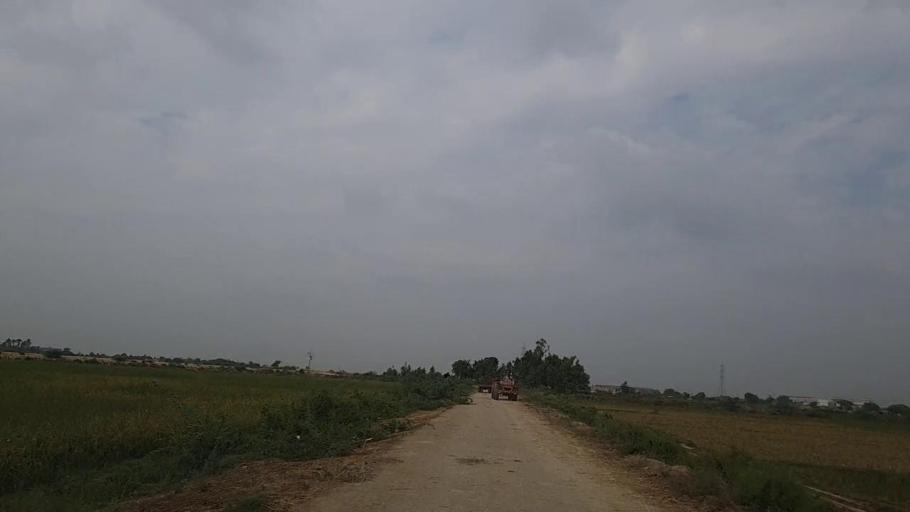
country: PK
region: Sindh
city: Mirpur Batoro
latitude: 24.6087
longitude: 68.0941
